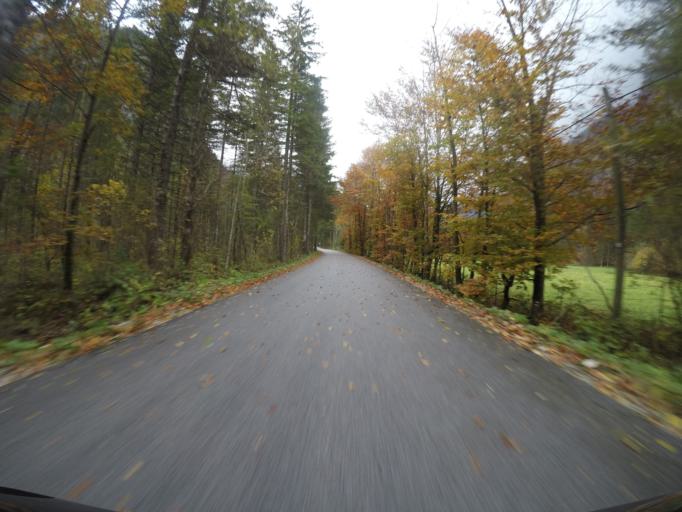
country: SI
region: Jesenice
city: Hrusica
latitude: 46.4123
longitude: 13.9943
